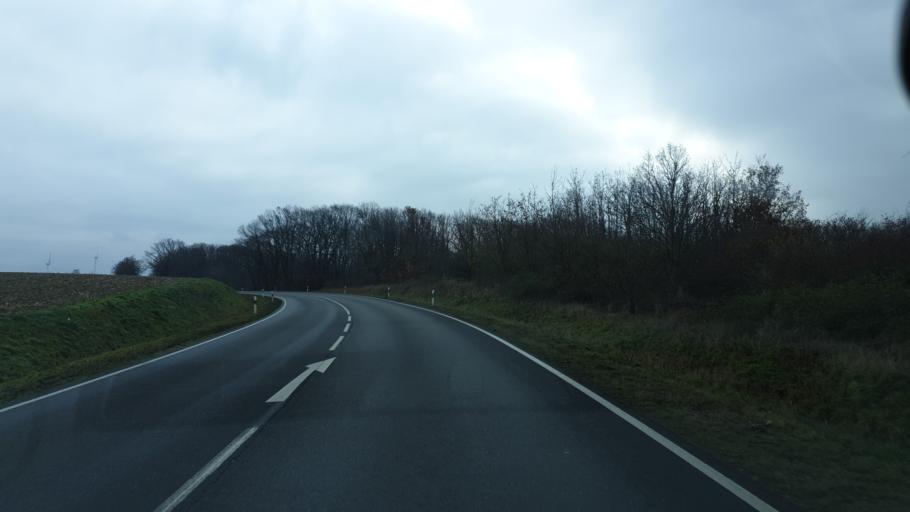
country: DE
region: Saxony-Anhalt
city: Stossen
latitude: 51.1261
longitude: 11.8964
